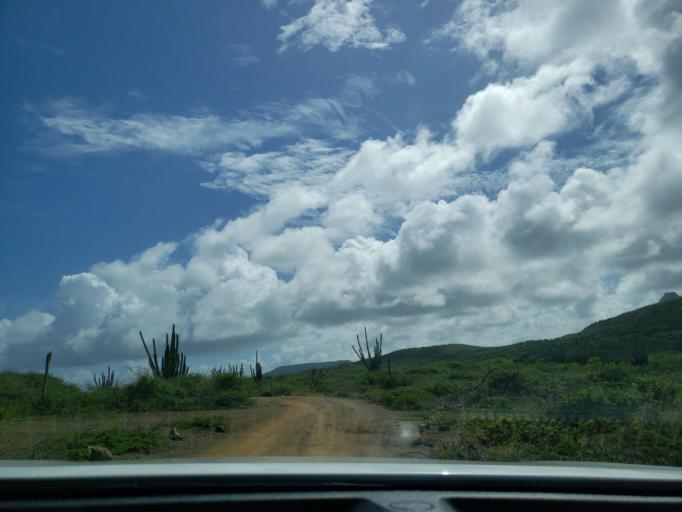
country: CW
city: Barber
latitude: 12.3648
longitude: -69.1163
